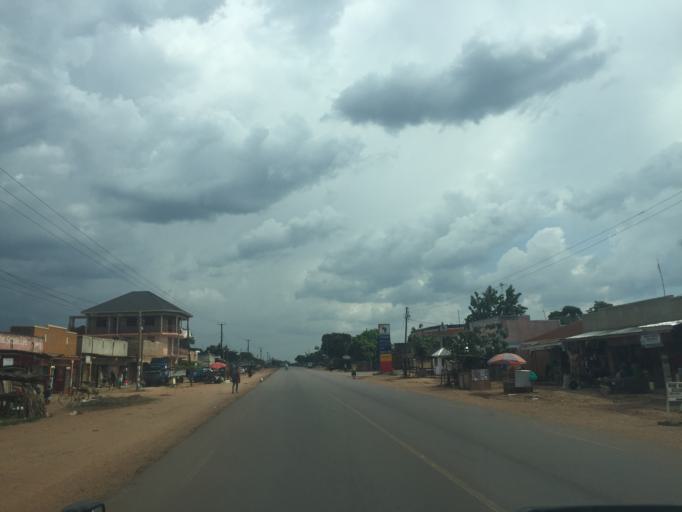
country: UG
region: Central Region
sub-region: Luwero District
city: Wobulenzi
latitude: 0.6817
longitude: 32.5246
